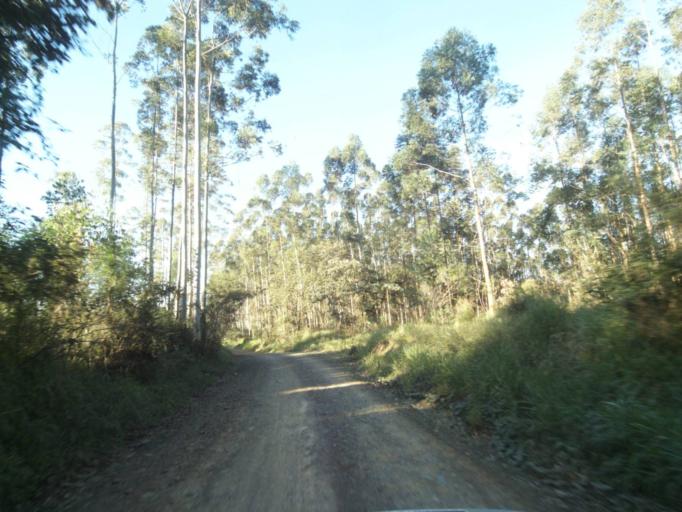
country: BR
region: Parana
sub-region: Telemaco Borba
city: Telemaco Borba
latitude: -24.4929
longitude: -50.5973
